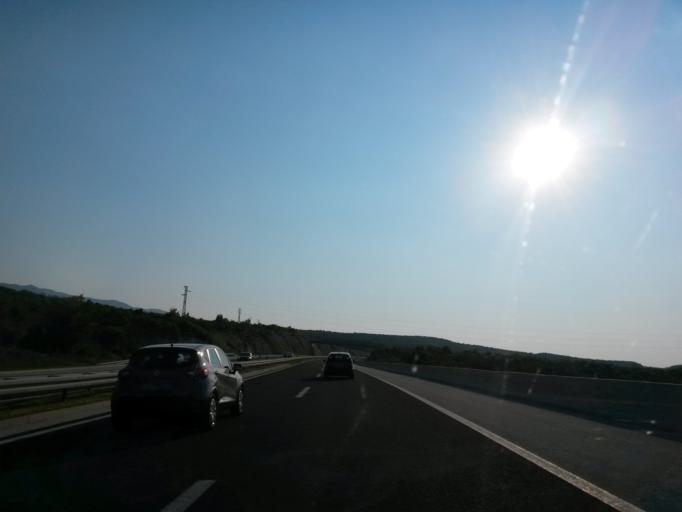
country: HR
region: Splitsko-Dalmatinska
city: Greda
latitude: 43.5824
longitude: 16.6552
